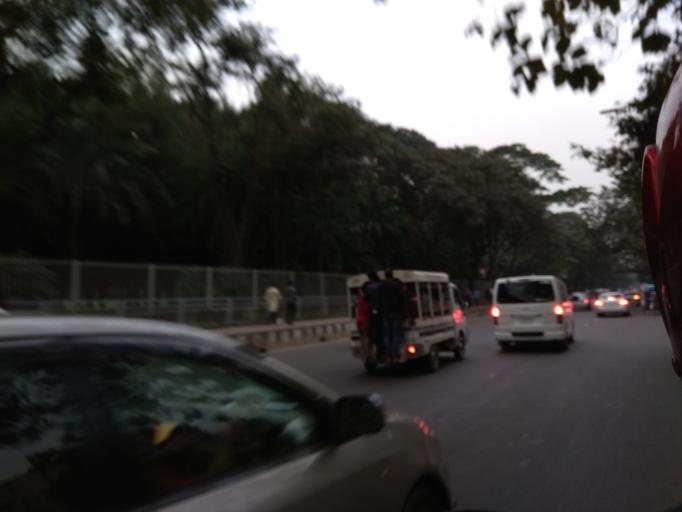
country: BD
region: Dhaka
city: Azimpur
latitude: 23.7609
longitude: 90.3836
